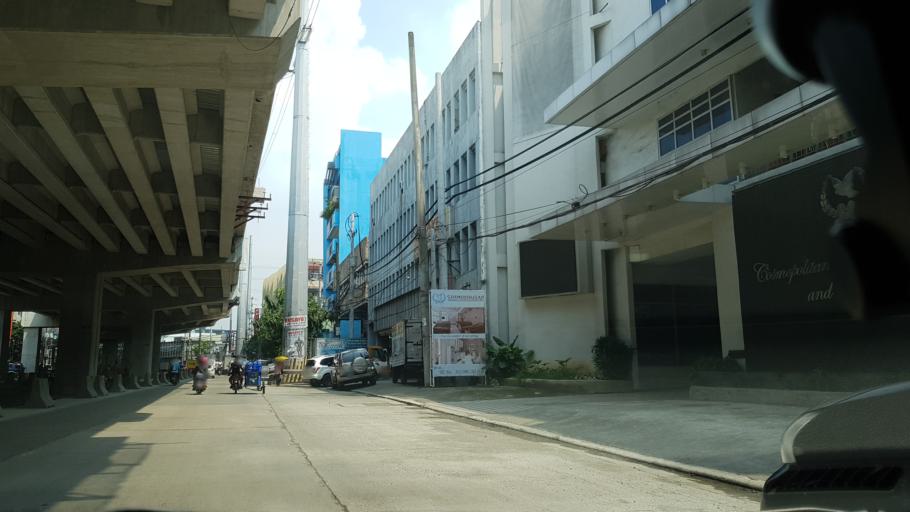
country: PH
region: Metro Manila
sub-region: San Juan
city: San Juan
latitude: 14.6137
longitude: 121.0170
